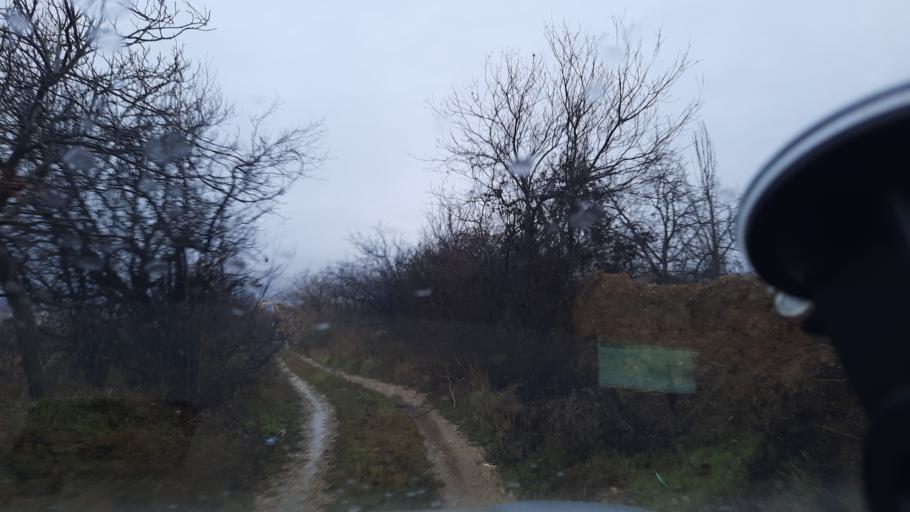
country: MK
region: Opstina Lipkovo
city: Matejche
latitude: 42.1225
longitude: 21.5990
